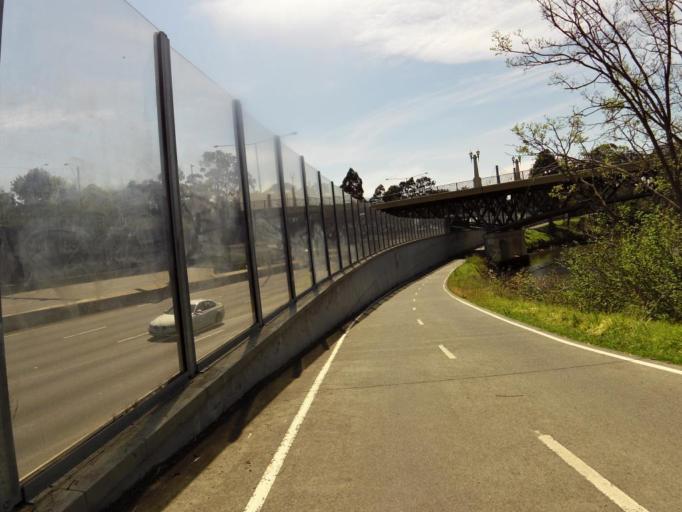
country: AU
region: Victoria
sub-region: Stonnington
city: Toorak
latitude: -37.8305
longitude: 145.0118
